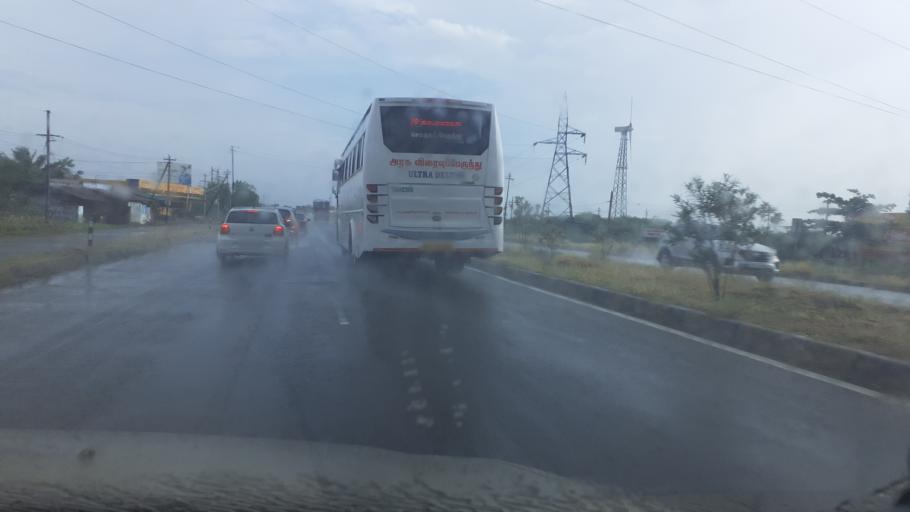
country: IN
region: Tamil Nadu
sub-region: Tirunelveli Kattabo
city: Gangaikondan
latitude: 8.8863
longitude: 77.7691
